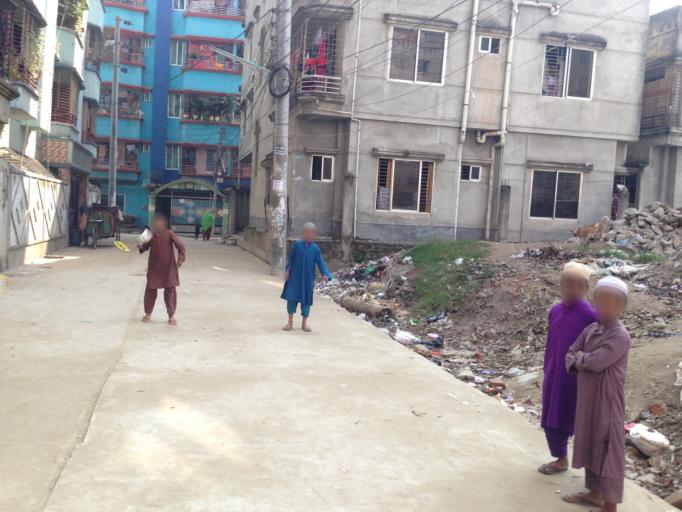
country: BD
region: Dhaka
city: Azimpur
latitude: 23.8020
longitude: 90.3464
